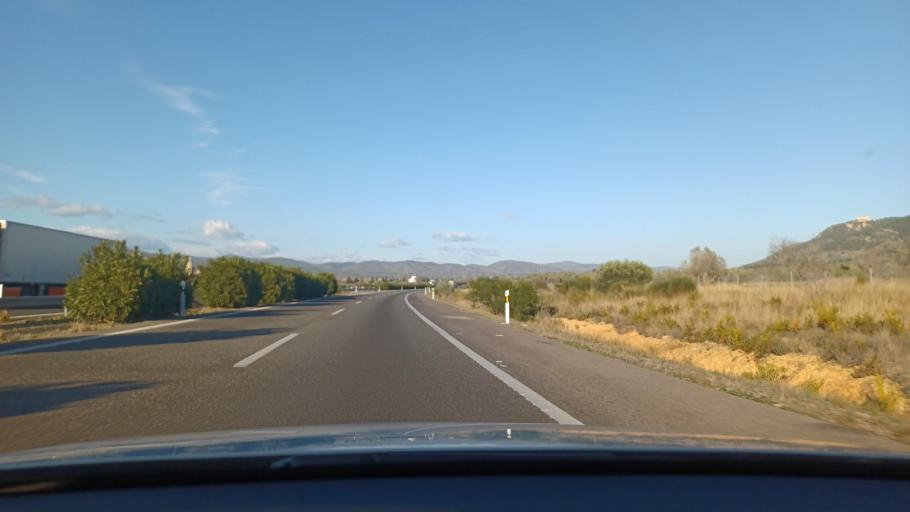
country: ES
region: Valencia
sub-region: Provincia de Castello
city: Alcala de Xivert
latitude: 40.2878
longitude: 0.2290
